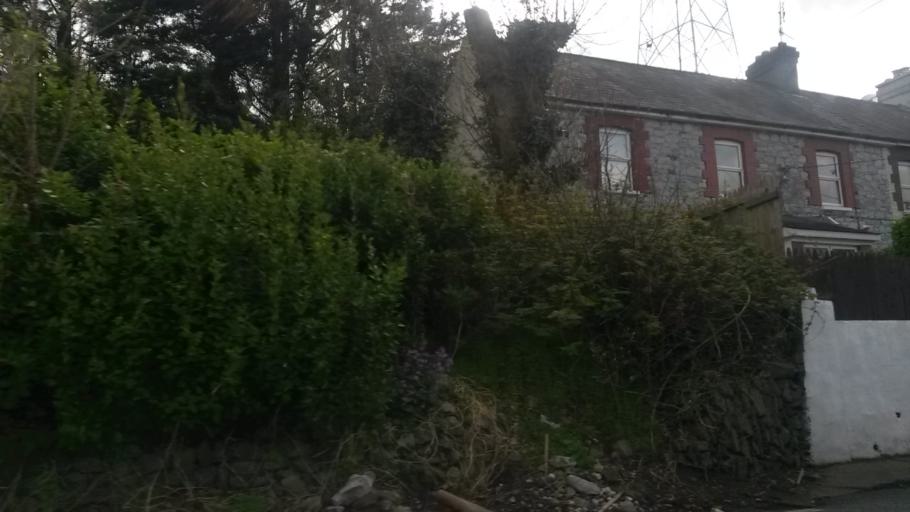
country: IE
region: Munster
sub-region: County Cork
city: Passage West
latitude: 51.8535
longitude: -8.3270
